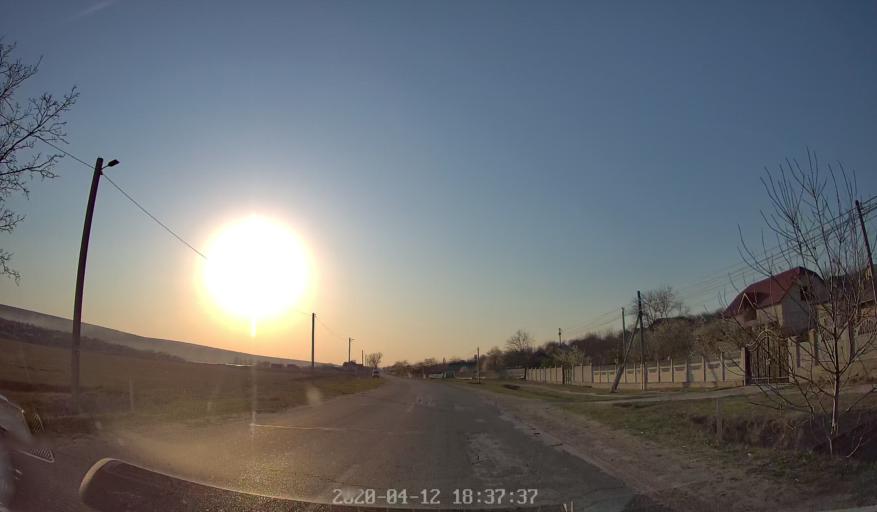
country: MD
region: Chisinau
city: Vadul lui Voda
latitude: 47.1219
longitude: 29.0126
